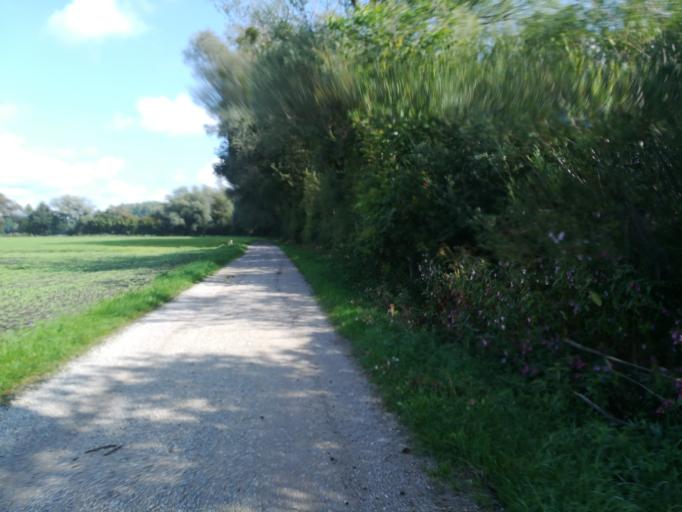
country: DE
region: Bavaria
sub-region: Upper Bavaria
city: Karlsfeld
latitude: 48.2259
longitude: 11.4998
